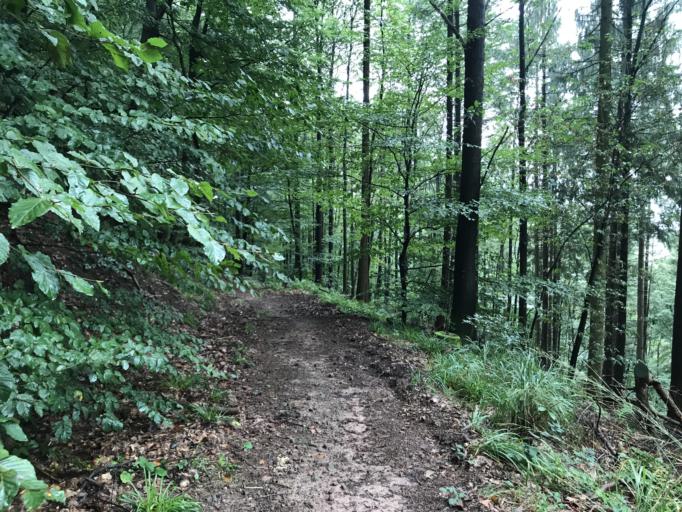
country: DE
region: Baden-Wuerttemberg
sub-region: Karlsruhe Region
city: Heidelberg
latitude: 49.4288
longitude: 8.7059
